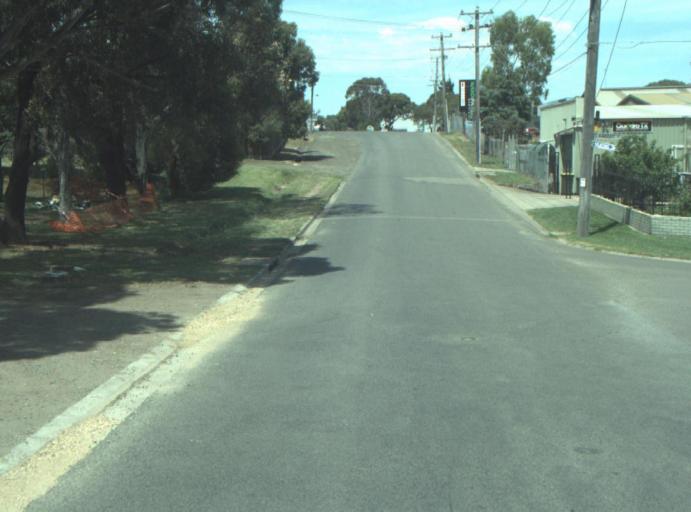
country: AU
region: Victoria
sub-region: Greater Geelong
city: Geelong West
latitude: -38.1600
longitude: 144.3398
